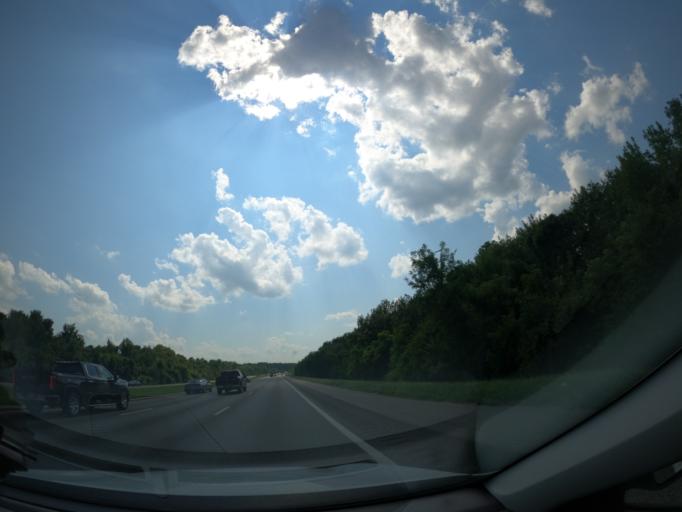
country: US
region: South Carolina
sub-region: Lexington County
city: Cayce
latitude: 33.9304
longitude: -81.0222
